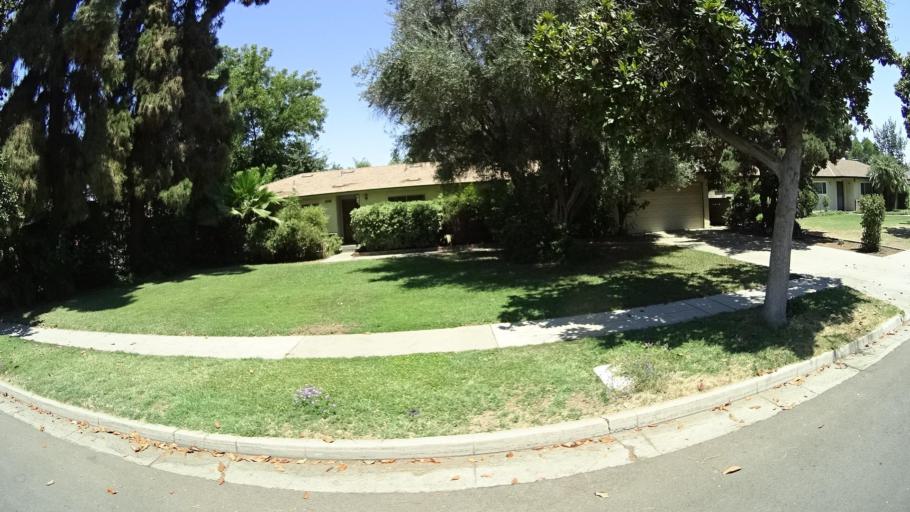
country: US
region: California
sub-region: Fresno County
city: Sunnyside
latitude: 36.7269
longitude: -119.7302
